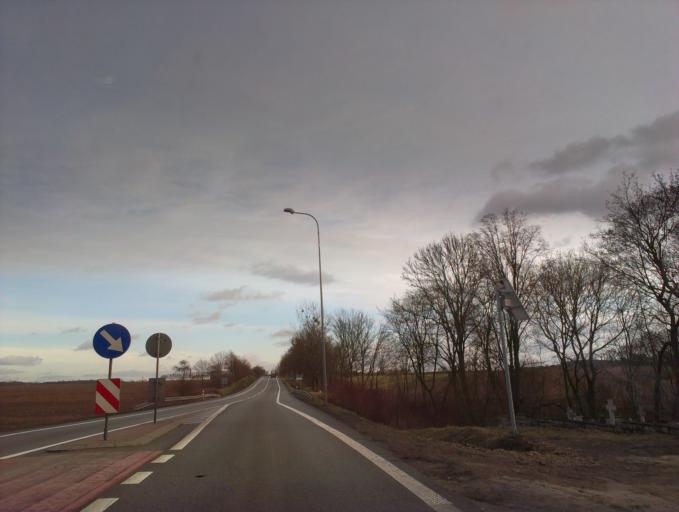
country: PL
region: Kujawsko-Pomorskie
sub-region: Powiat lipnowski
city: Lipno
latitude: 52.8575
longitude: 19.2548
